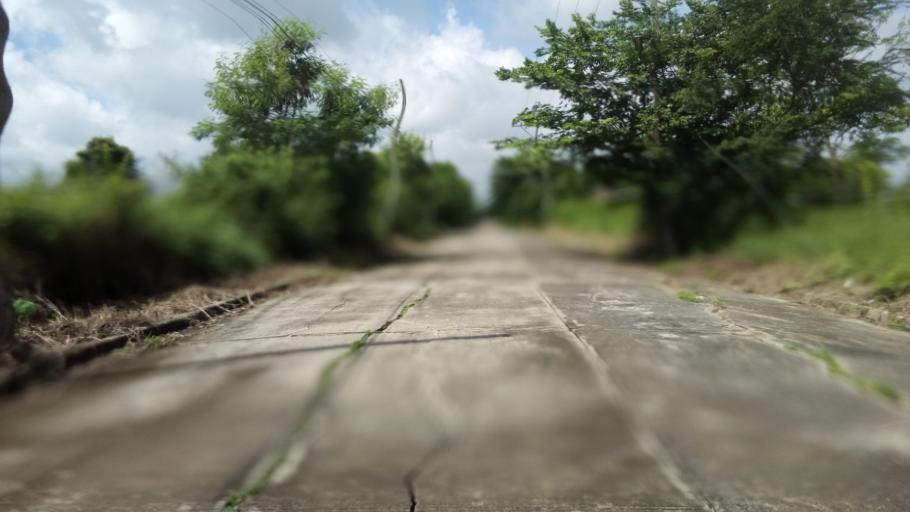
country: TH
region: Pathum Thani
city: Nong Suea
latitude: 14.0571
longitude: 100.8628
